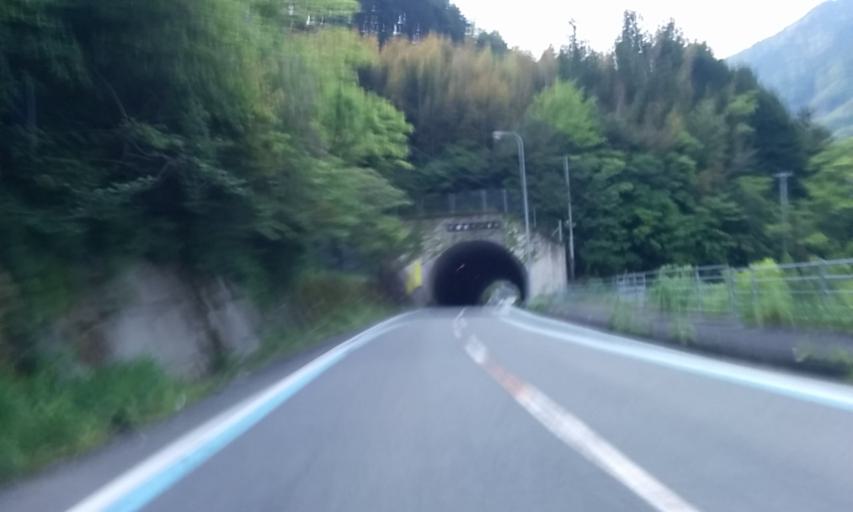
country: JP
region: Ehime
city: Saijo
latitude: 33.8443
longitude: 133.2181
